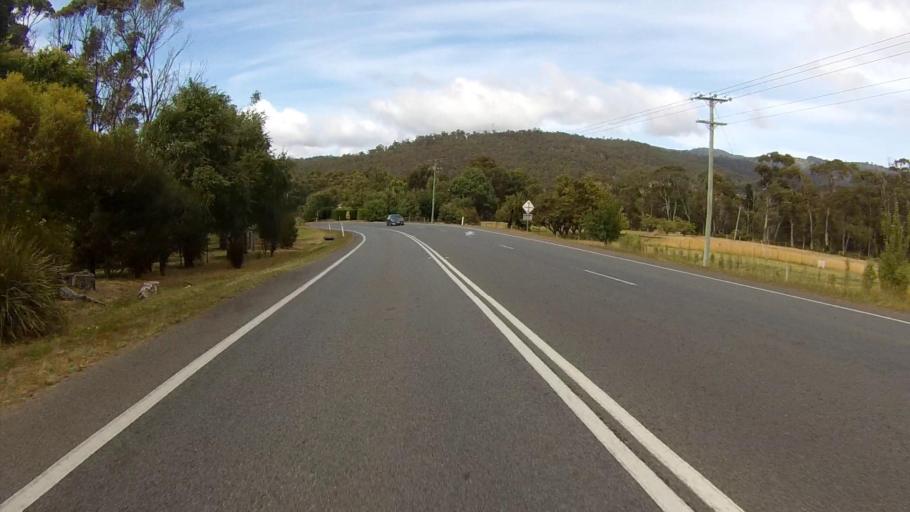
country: AU
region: Tasmania
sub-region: Kingborough
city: Kettering
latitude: -43.1181
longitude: 147.2440
